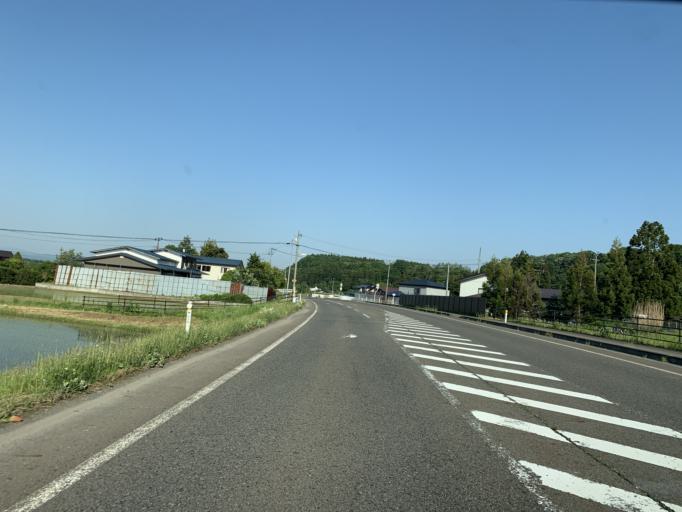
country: JP
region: Iwate
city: Kitakami
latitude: 39.2834
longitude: 141.0189
